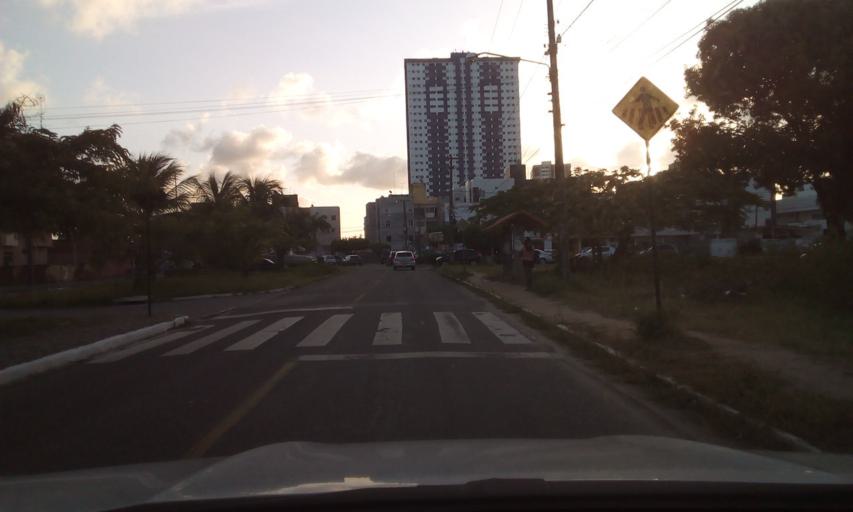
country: BR
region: Paraiba
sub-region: Joao Pessoa
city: Joao Pessoa
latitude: -7.0769
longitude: -34.8382
